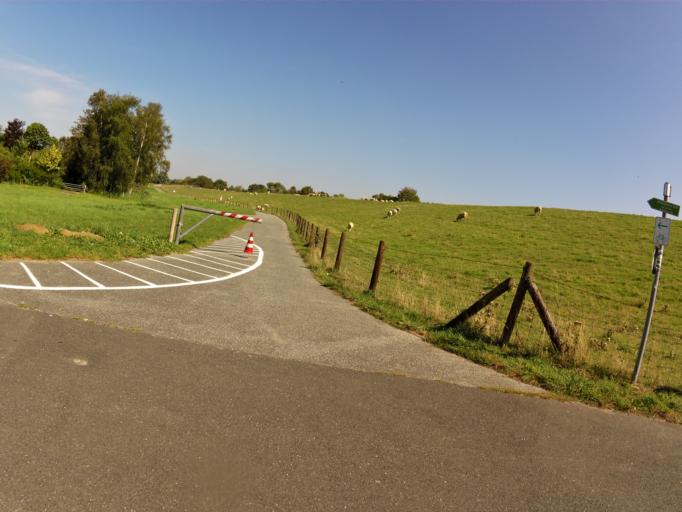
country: DE
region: Lower Saxony
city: Brake (Unterweser)
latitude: 53.2918
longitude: 8.4835
